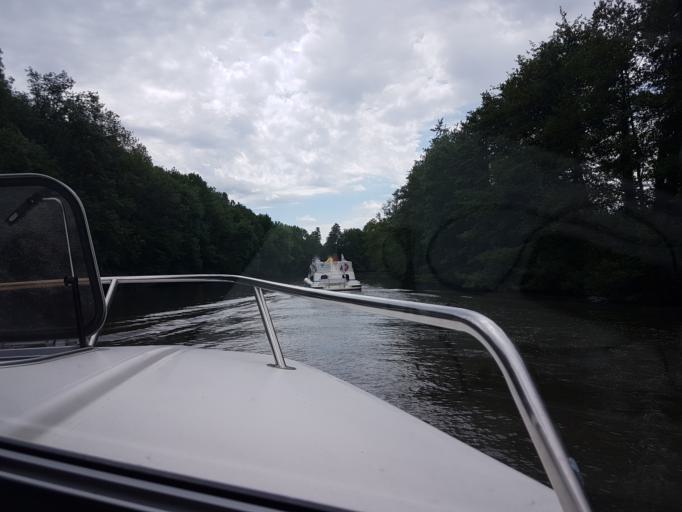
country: FR
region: Bourgogne
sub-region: Departement de la Nievre
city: Clamecy
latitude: 47.4671
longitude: 3.5282
